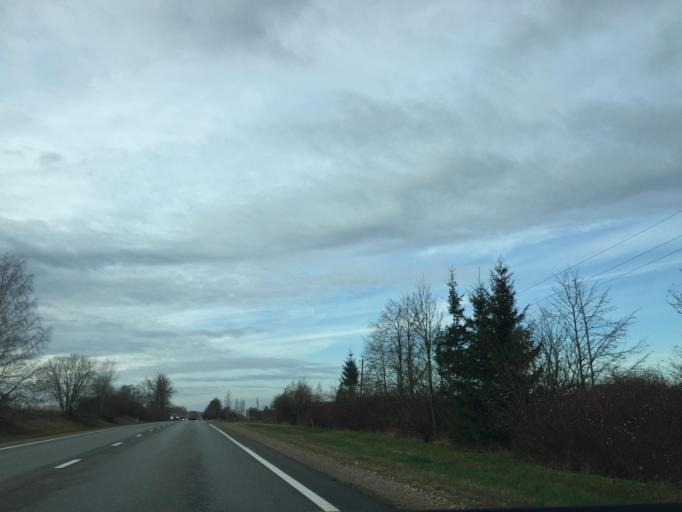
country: LV
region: Jaunpils
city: Jaunpils
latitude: 56.6661
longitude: 23.0477
